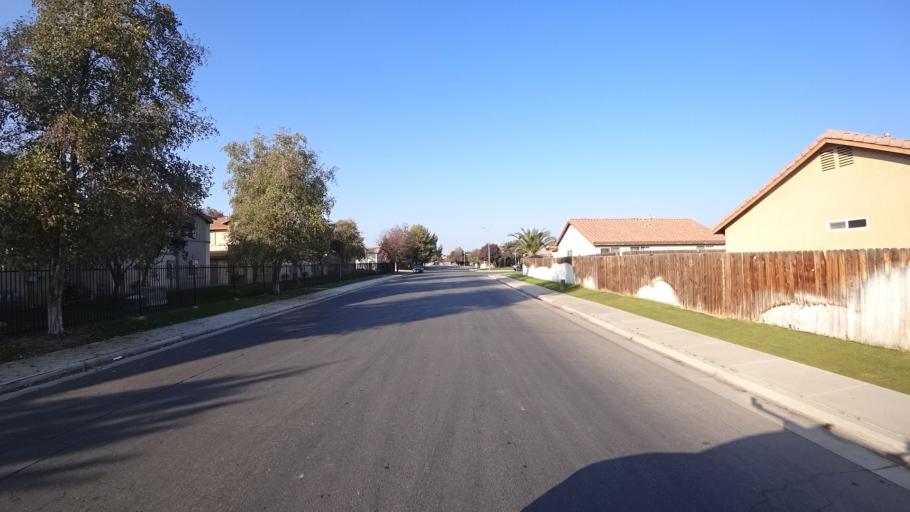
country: US
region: California
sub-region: Kern County
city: Greenfield
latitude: 35.2834
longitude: -119.0074
